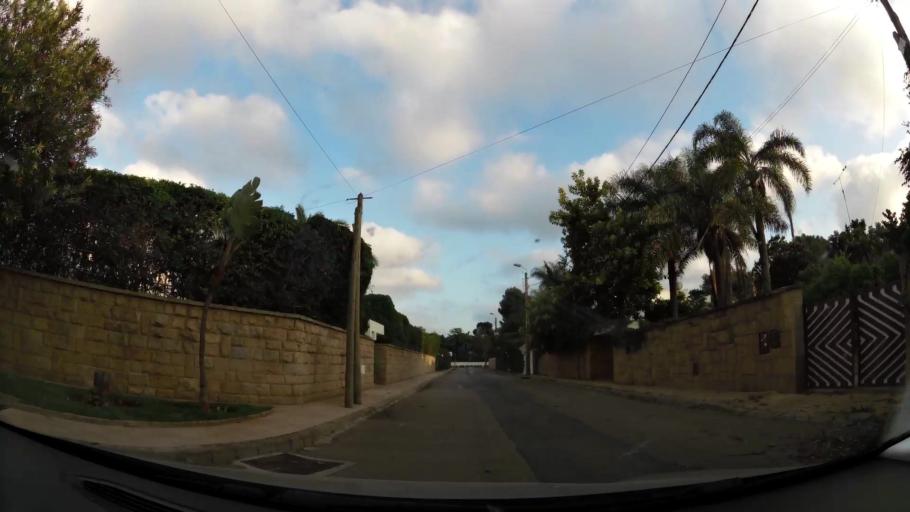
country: MA
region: Rabat-Sale-Zemmour-Zaer
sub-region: Rabat
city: Rabat
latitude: 33.9601
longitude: -6.8310
